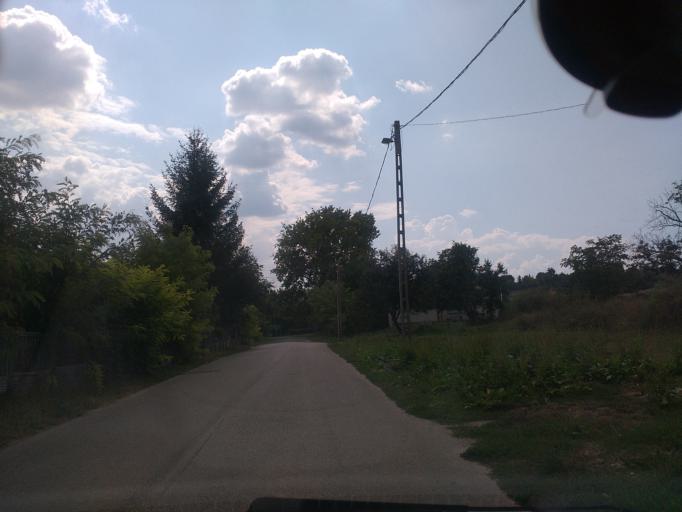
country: HU
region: Komarom-Esztergom
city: Pilismarot
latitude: 47.7886
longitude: 18.8756
